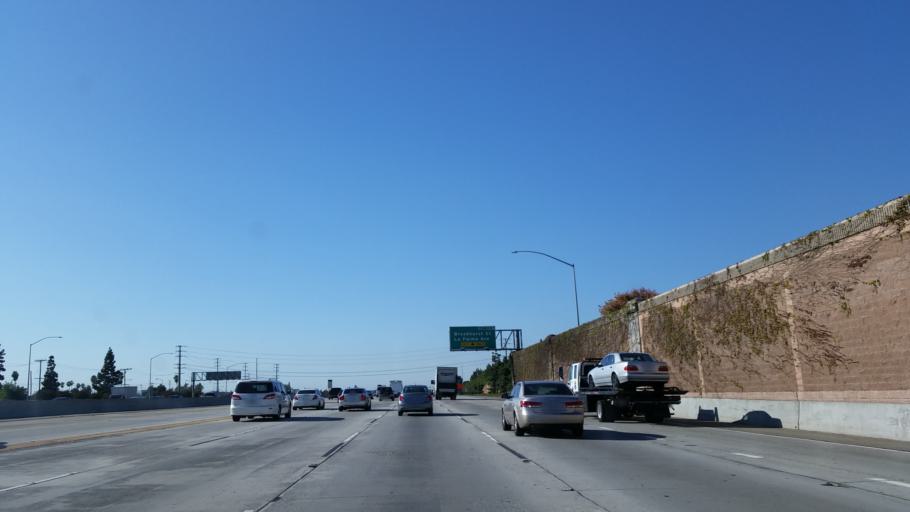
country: US
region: California
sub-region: Orange County
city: Anaheim
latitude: 33.8379
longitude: -117.9451
